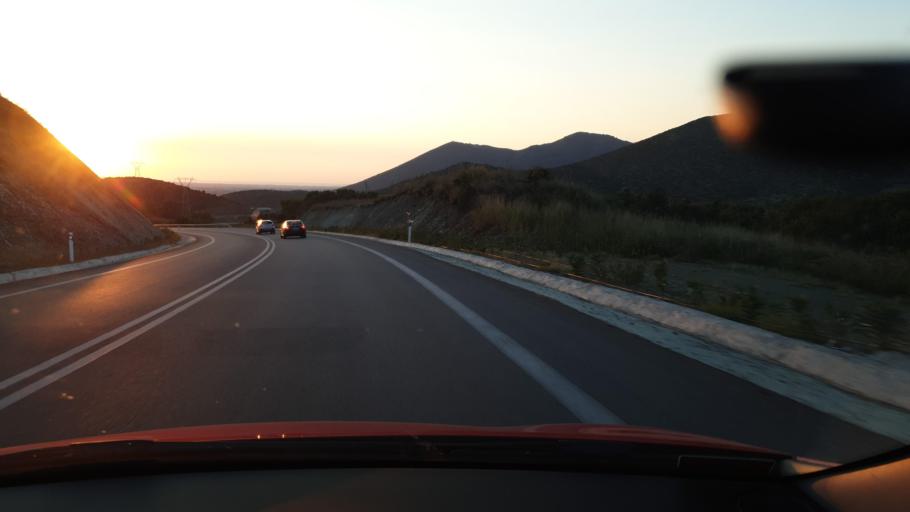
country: GR
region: Central Macedonia
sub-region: Nomos Chalkidikis
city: Galatista
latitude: 40.4637
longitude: 23.2198
